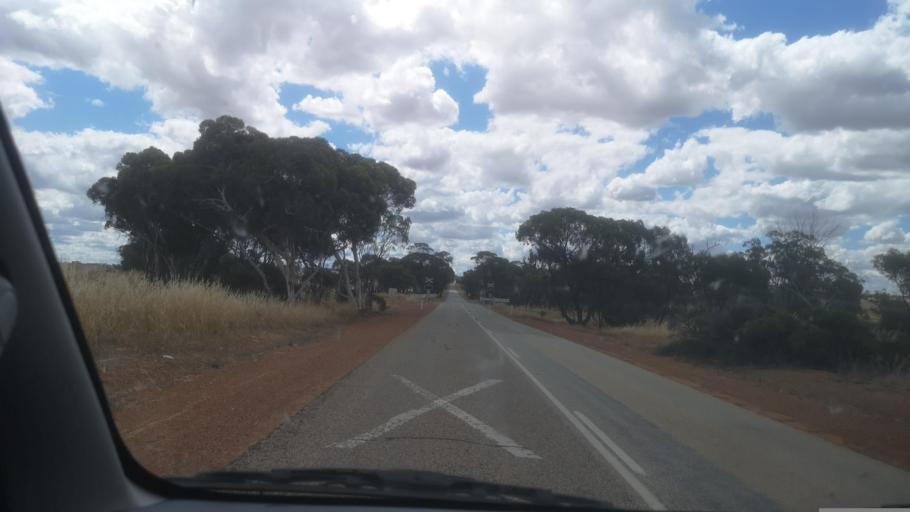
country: AU
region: Western Australia
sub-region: Beverley
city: Beverley
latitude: -31.9811
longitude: 117.0884
